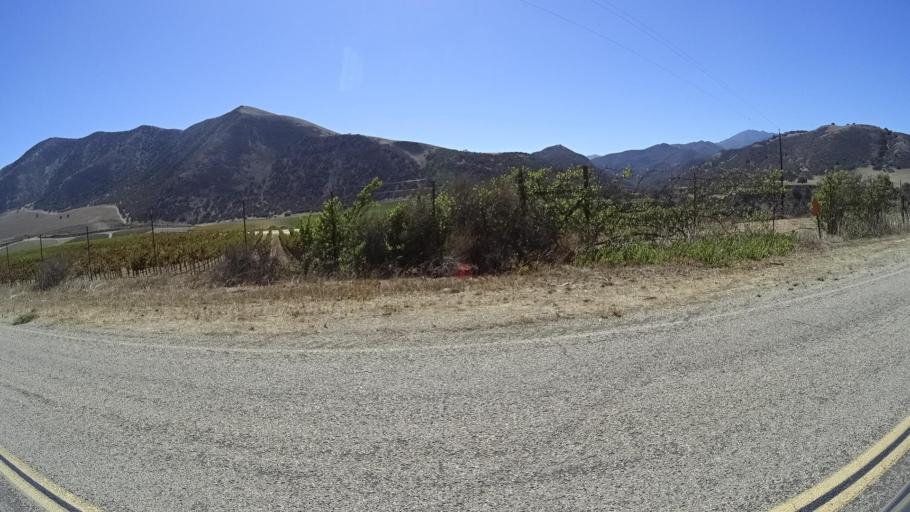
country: US
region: California
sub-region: Monterey County
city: Greenfield
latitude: 36.2710
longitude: -121.3369
